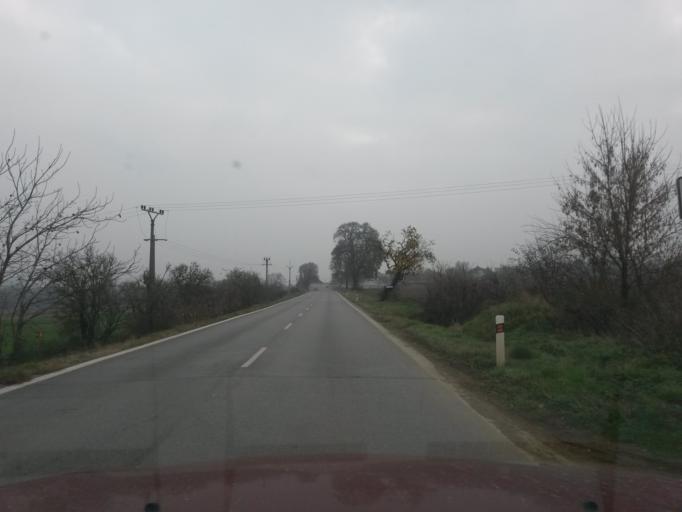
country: SK
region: Kosicky
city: Kosice
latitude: 48.8332
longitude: 21.2891
